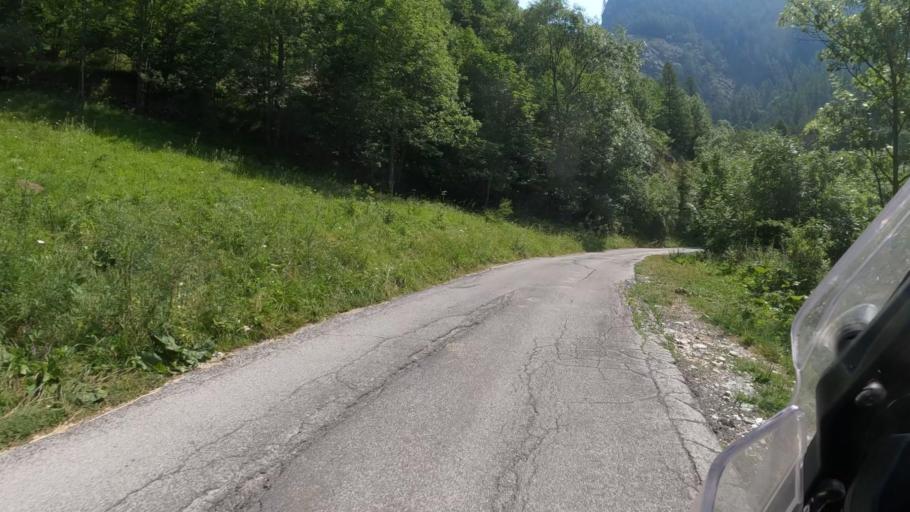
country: IT
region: Piedmont
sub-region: Provincia di Cuneo
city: Canosio
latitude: 44.4424
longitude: 7.0612
